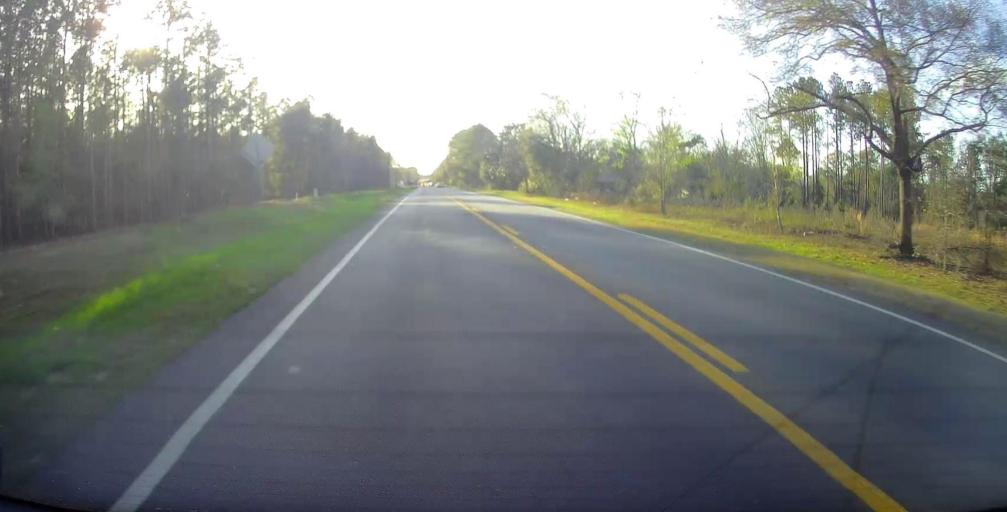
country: US
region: Georgia
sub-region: Evans County
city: Claxton
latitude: 32.1601
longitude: -81.8667
